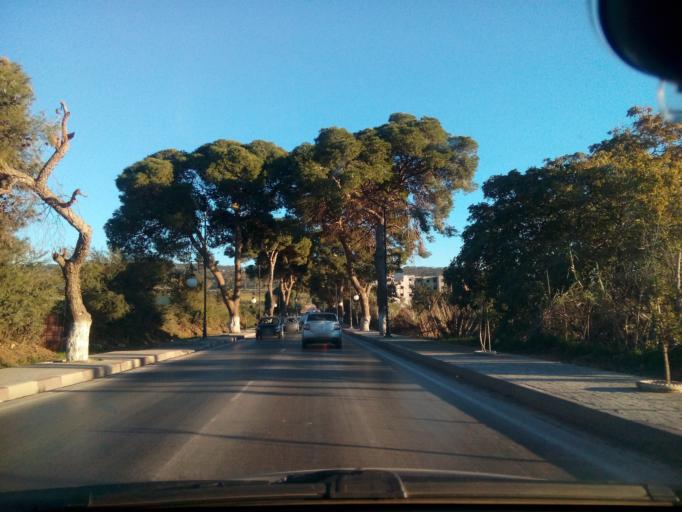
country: DZ
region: Mostaganem
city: Mostaganem
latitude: 35.7763
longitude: 0.1956
